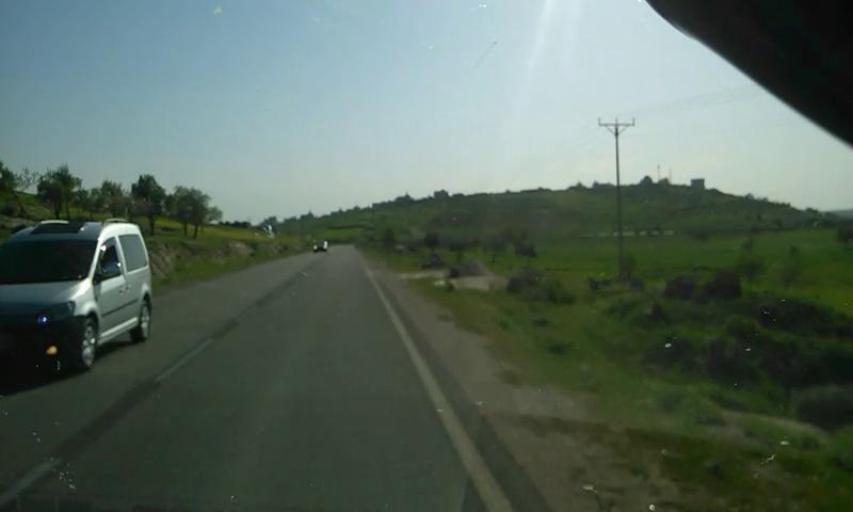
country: PS
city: Al Hilah
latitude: 31.4747
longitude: 35.1323
